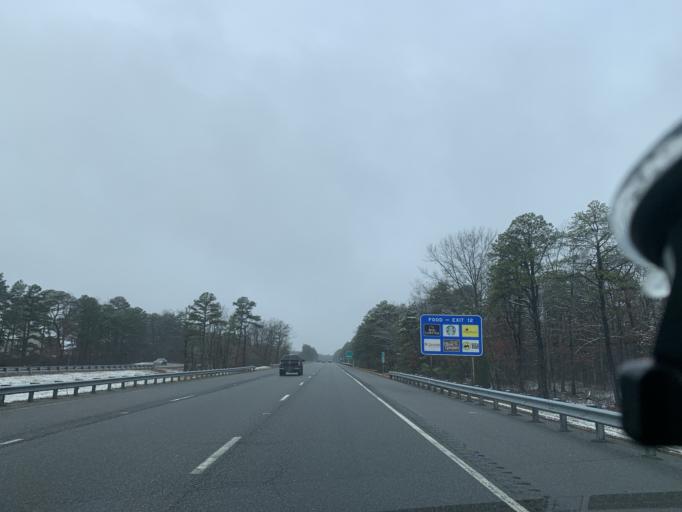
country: US
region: New Jersey
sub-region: Atlantic County
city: Pomona
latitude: 39.4421
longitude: -74.6073
